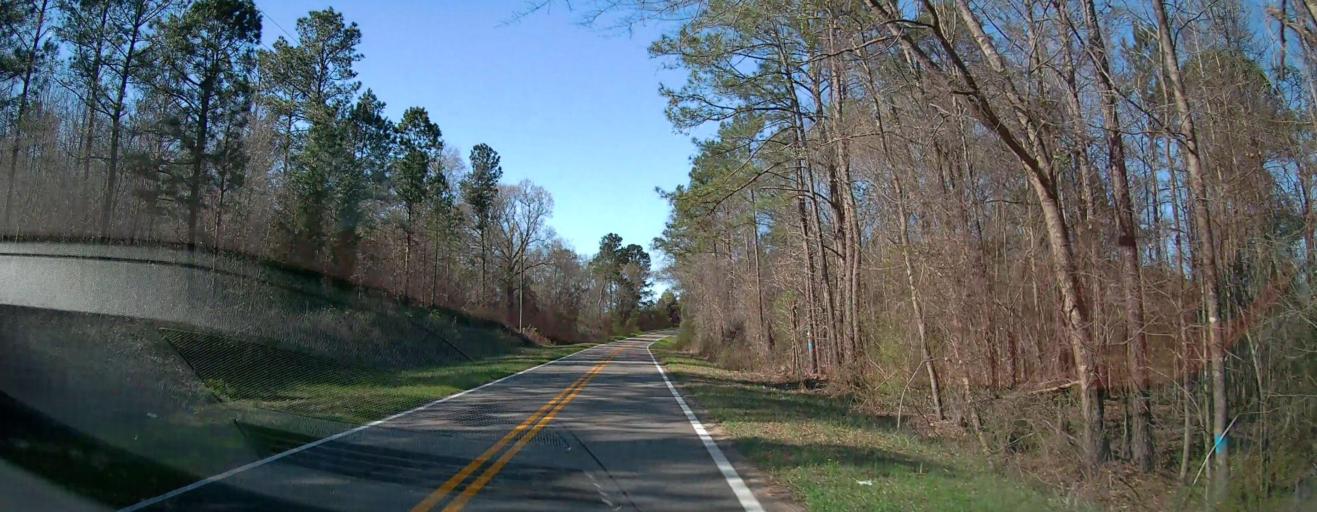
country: US
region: Georgia
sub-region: Peach County
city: Fort Valley
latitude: 32.6133
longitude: -83.9187
